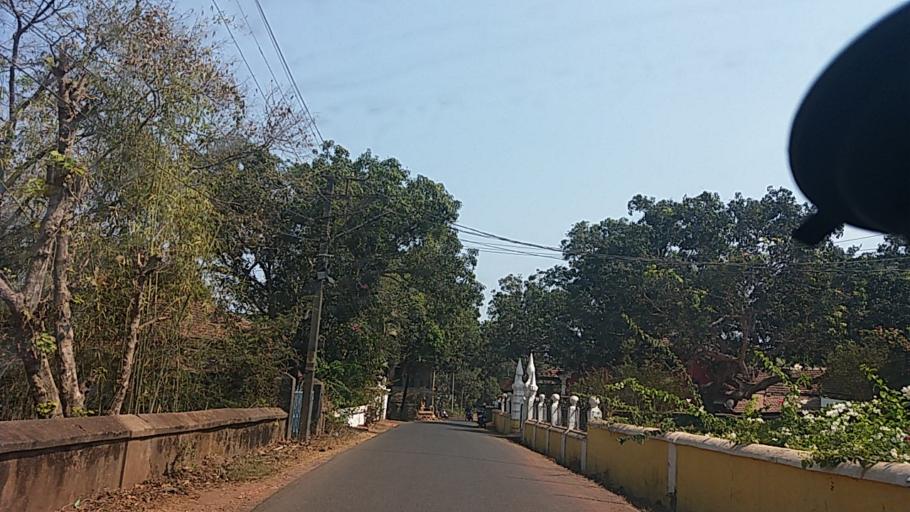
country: IN
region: Goa
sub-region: North Goa
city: Saligao
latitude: 15.5406
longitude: 73.7837
